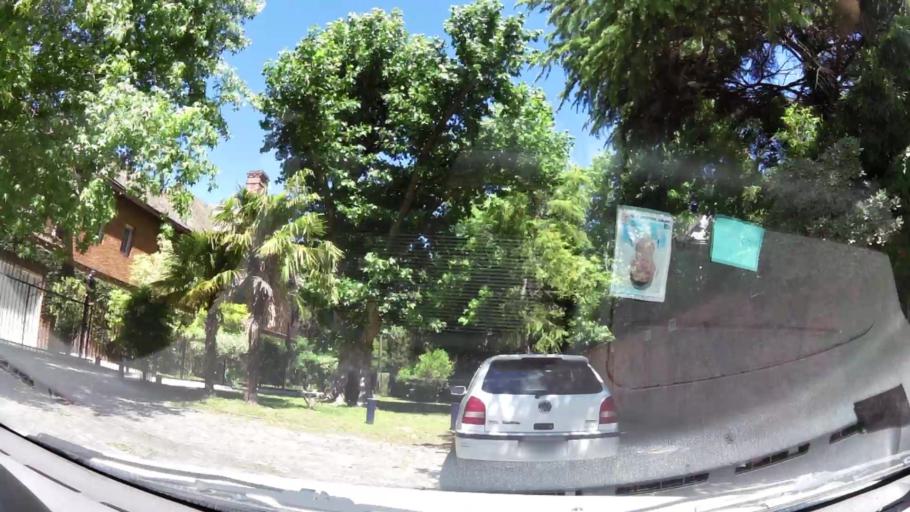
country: AR
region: Buenos Aires
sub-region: Partido de San Isidro
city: San Isidro
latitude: -34.4777
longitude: -58.4943
